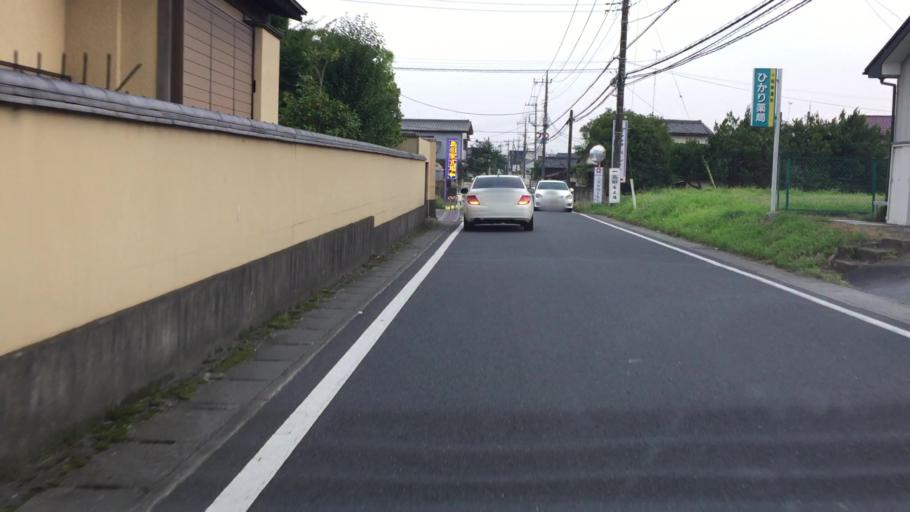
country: JP
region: Tochigi
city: Tochigi
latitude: 36.3926
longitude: 139.7204
